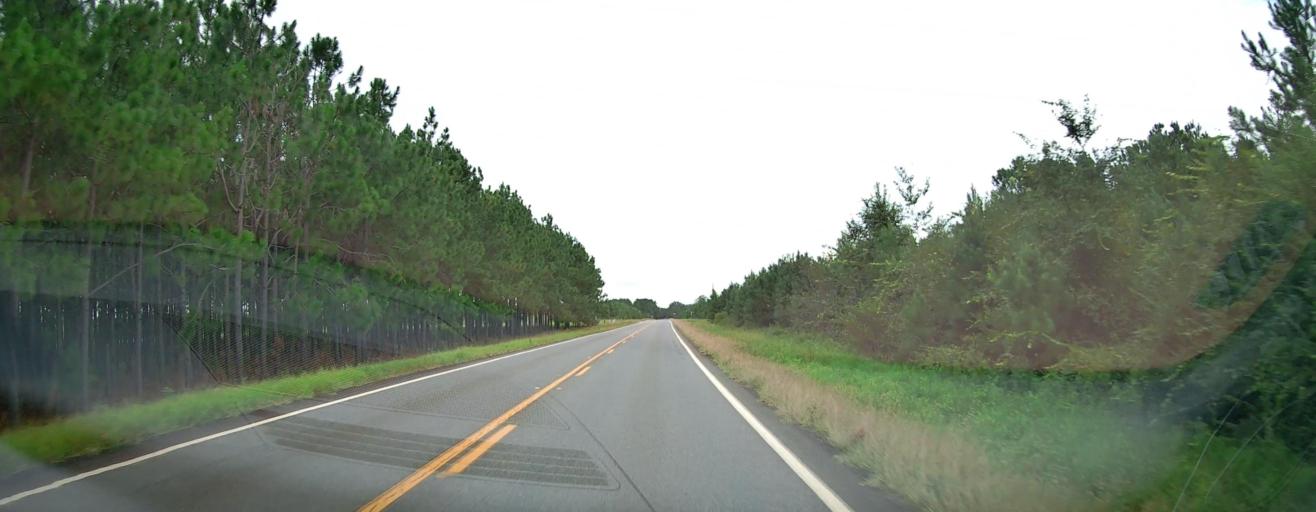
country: US
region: Georgia
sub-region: Marion County
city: Buena Vista
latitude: 32.2671
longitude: -84.4303
